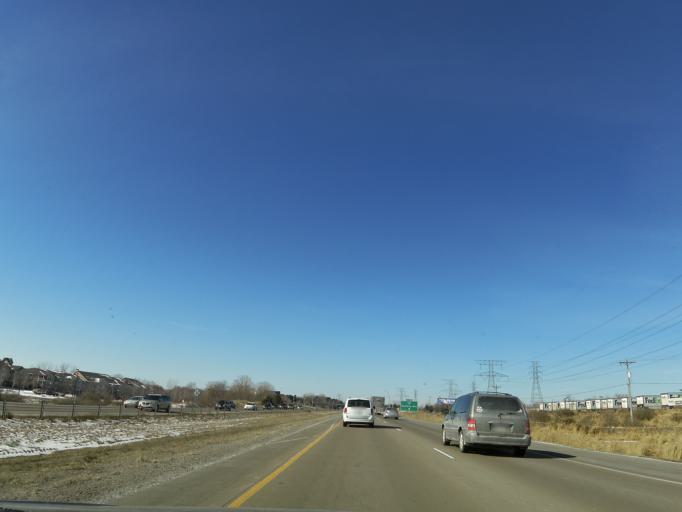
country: US
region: Minnesota
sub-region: Ramsey County
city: North Saint Paul
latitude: 45.0334
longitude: -92.9752
